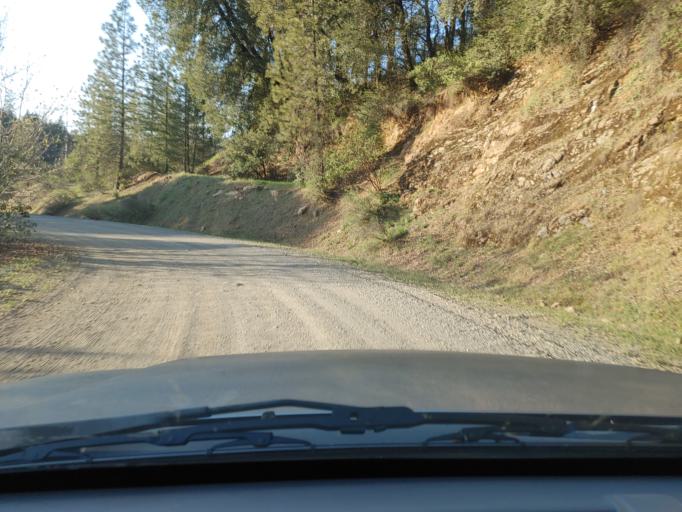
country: US
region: California
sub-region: Shasta County
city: Bella Vista
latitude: 40.8369
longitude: -122.0175
